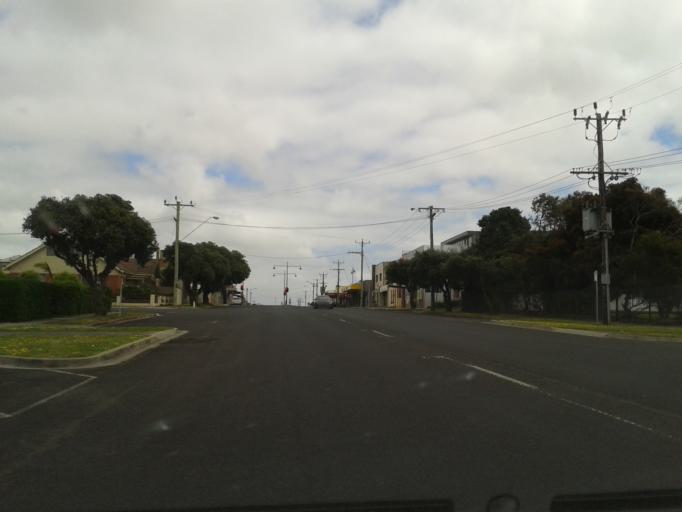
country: AU
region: Victoria
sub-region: Glenelg
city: Portland
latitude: -38.3464
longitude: 141.6057
